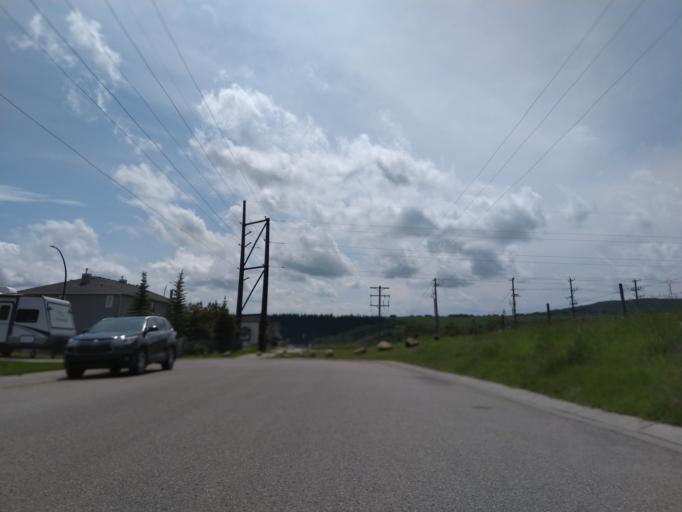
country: CA
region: Alberta
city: Cochrane
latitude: 51.1841
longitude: -114.5133
